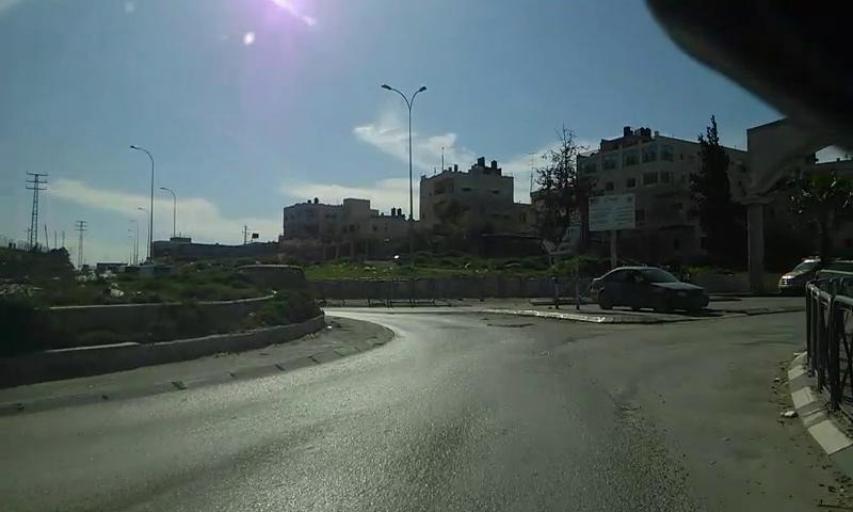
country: PS
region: West Bank
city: Ar Ram wa Dahiyat al Barid
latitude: 31.8564
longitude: 35.2404
